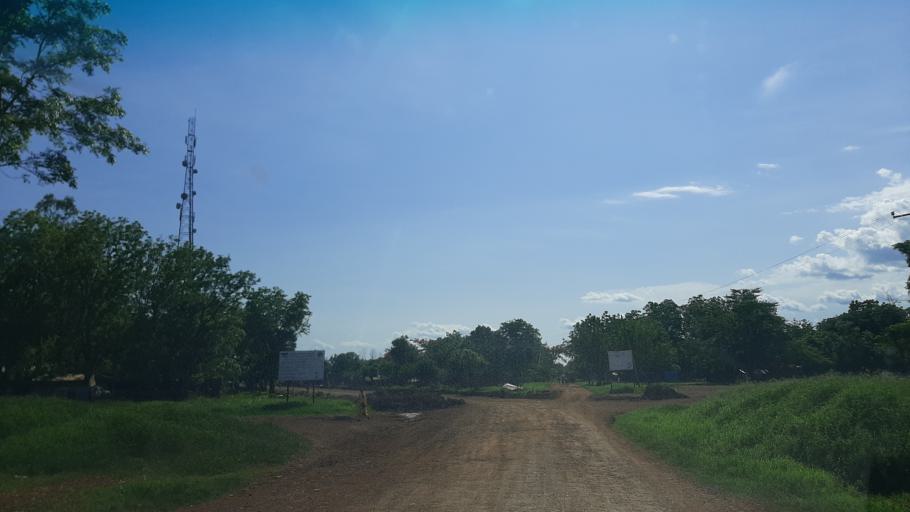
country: ET
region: Gambela
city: Gambela
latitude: 7.8975
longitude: 34.5448
